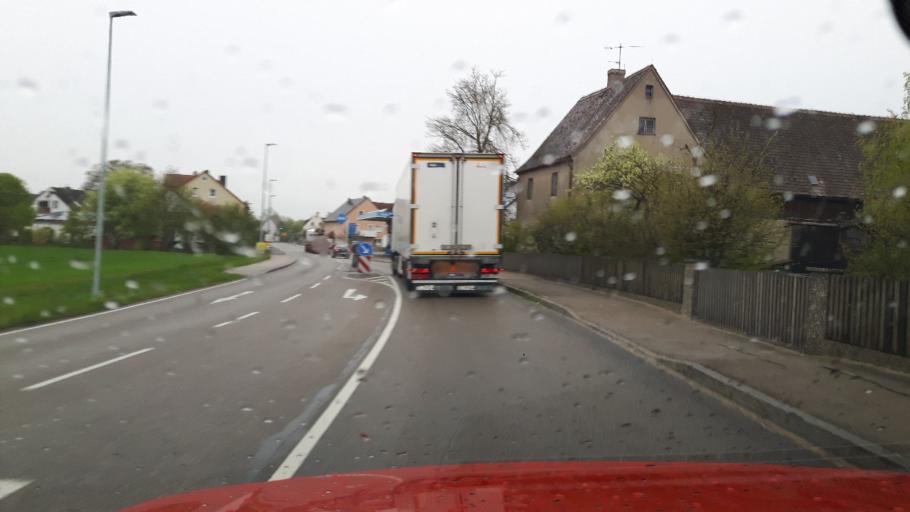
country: DE
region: Bavaria
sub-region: Regierungsbezirk Mittelfranken
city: Merkendorf
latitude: 49.1977
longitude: 10.7028
